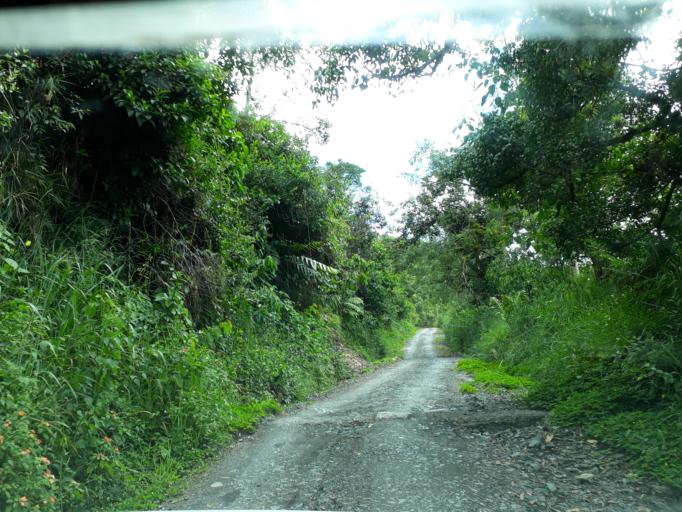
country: CO
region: Boyaca
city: Quipama
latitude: 5.4235
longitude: -74.1816
